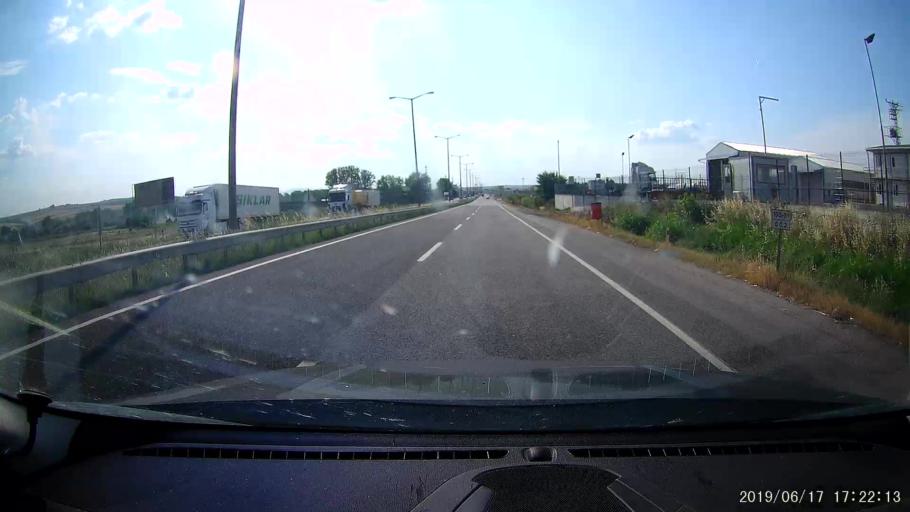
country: GR
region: East Macedonia and Thrace
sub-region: Nomos Evrou
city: Rizia
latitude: 41.7104
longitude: 26.3789
